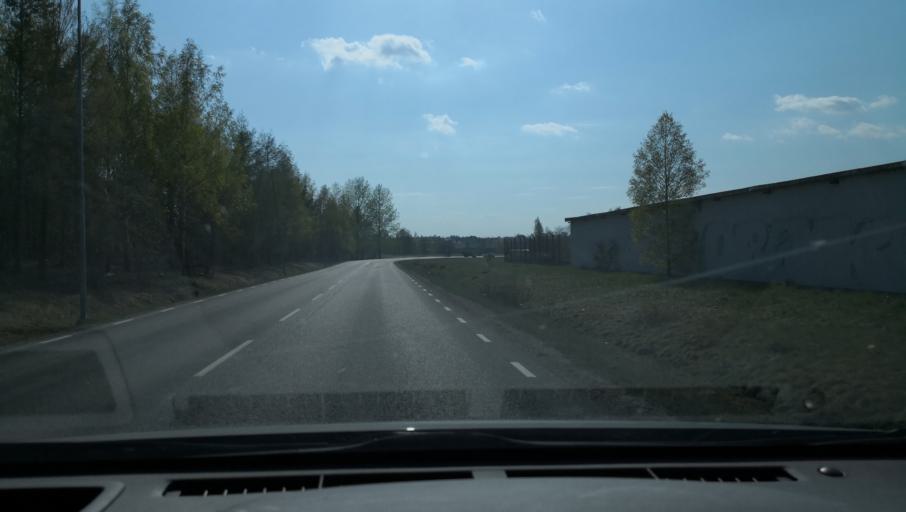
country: SE
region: Vaestmanland
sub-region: Sala Kommun
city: Sala
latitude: 59.9312
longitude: 16.6089
